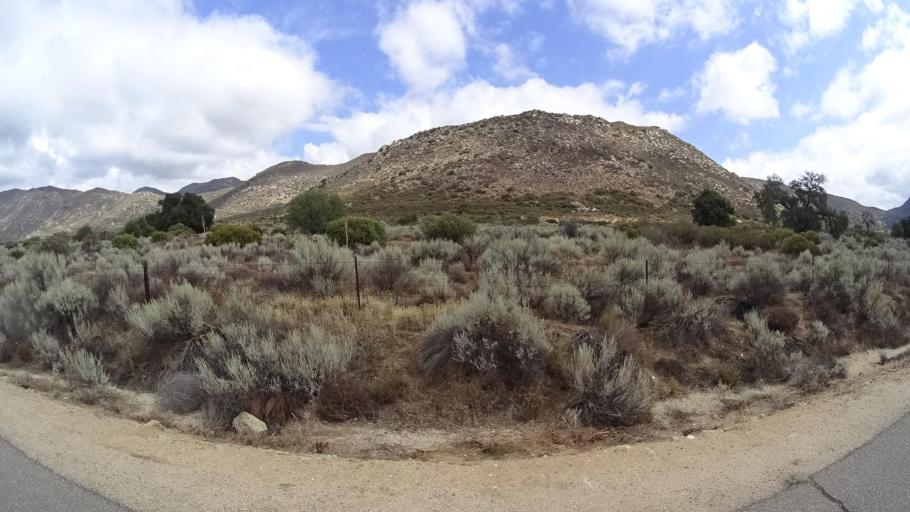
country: US
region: California
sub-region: San Diego County
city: Pine Valley
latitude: 32.7491
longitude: -116.4835
